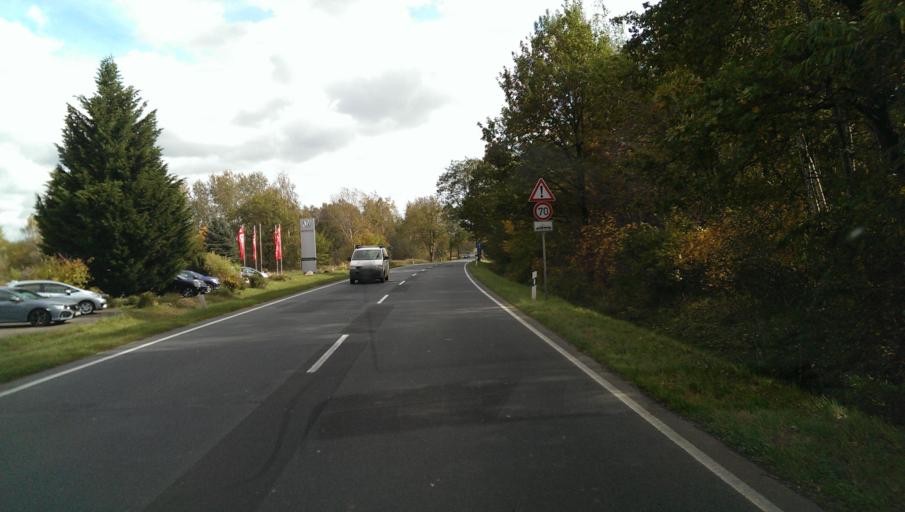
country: DE
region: Brandenburg
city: Schwarzheide
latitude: 51.4696
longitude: 13.8505
